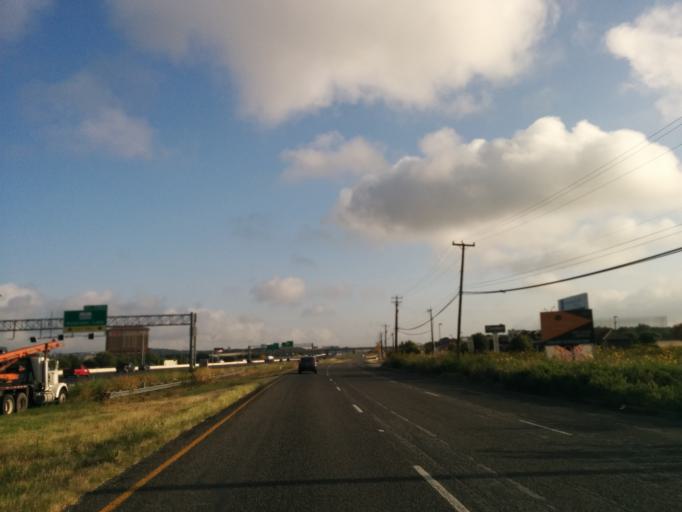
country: US
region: Texas
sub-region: Bexar County
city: Shavano Park
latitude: 29.5831
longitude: -98.5966
